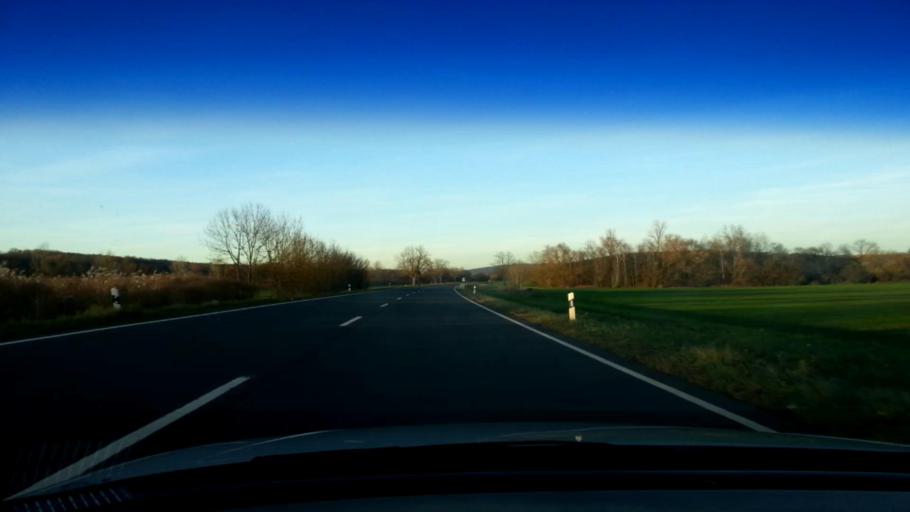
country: DE
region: Bavaria
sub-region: Upper Franconia
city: Rattelsdorf
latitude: 50.0258
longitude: 10.8824
